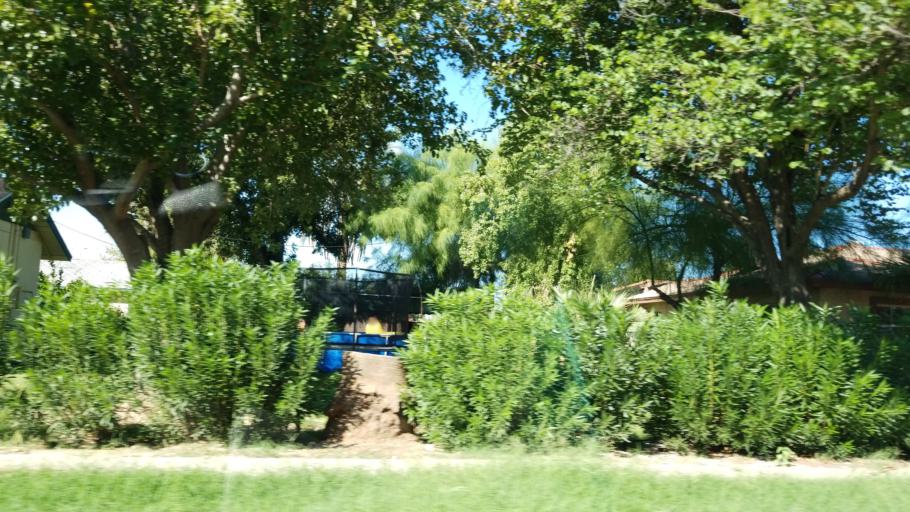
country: US
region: Arizona
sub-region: Maricopa County
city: Glendale
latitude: 33.5402
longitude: -112.1774
